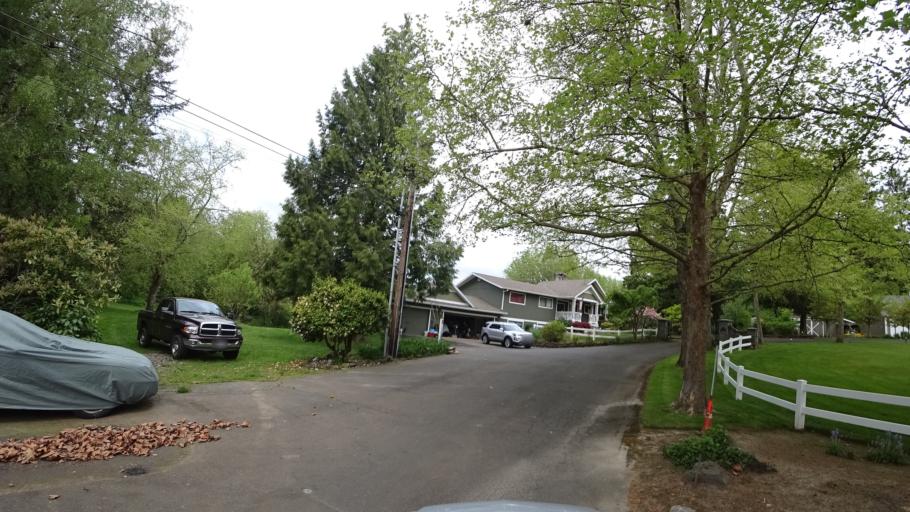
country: US
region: Oregon
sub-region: Washington County
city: Hillsboro
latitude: 45.5300
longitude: -123.0033
